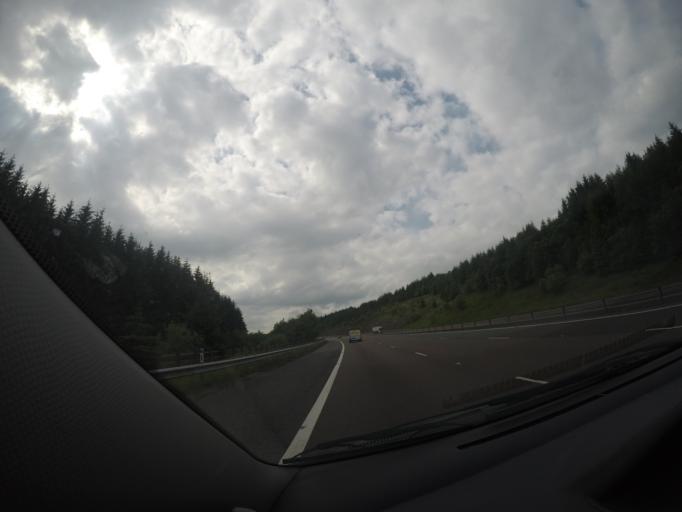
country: GB
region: Scotland
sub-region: Dumfries and Galloway
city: Moffat
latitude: 55.4076
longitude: -3.5610
